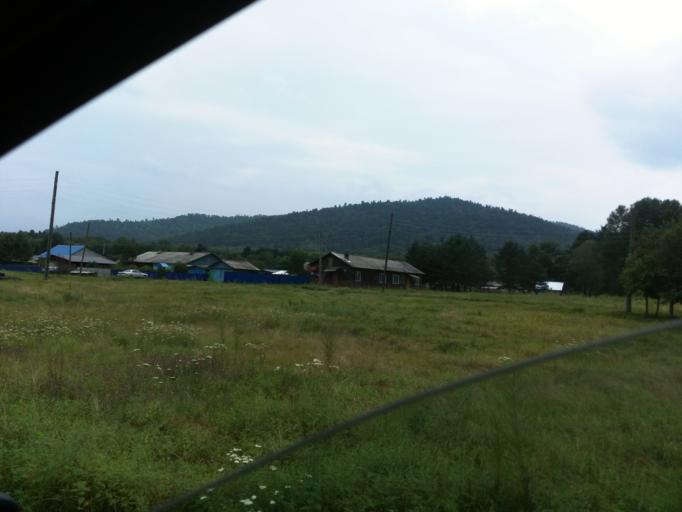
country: RU
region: Primorskiy
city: Krasnorechenskiy
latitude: 45.4350
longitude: 135.5215
